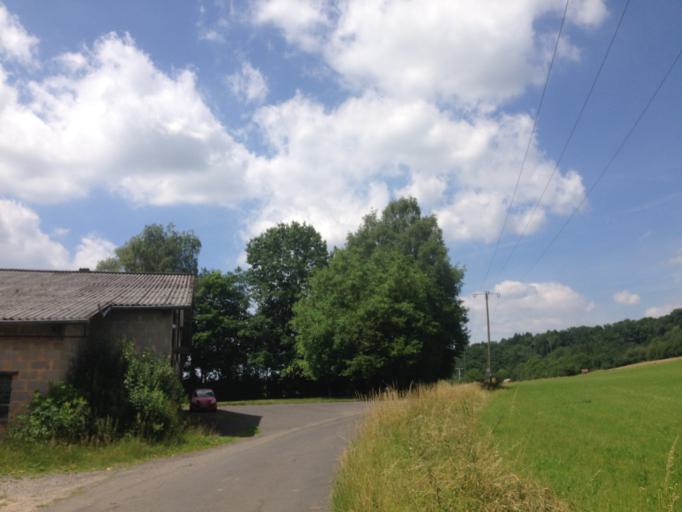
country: DE
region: Hesse
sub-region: Regierungsbezirk Giessen
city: Grunberg
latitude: 50.5999
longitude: 8.9134
